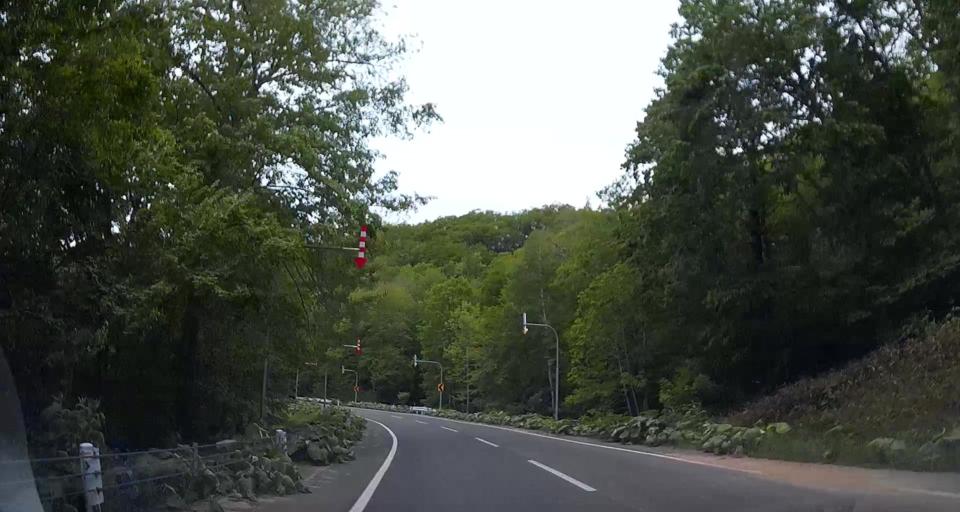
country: JP
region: Hokkaido
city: Chitose
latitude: 42.7922
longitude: 142.0572
